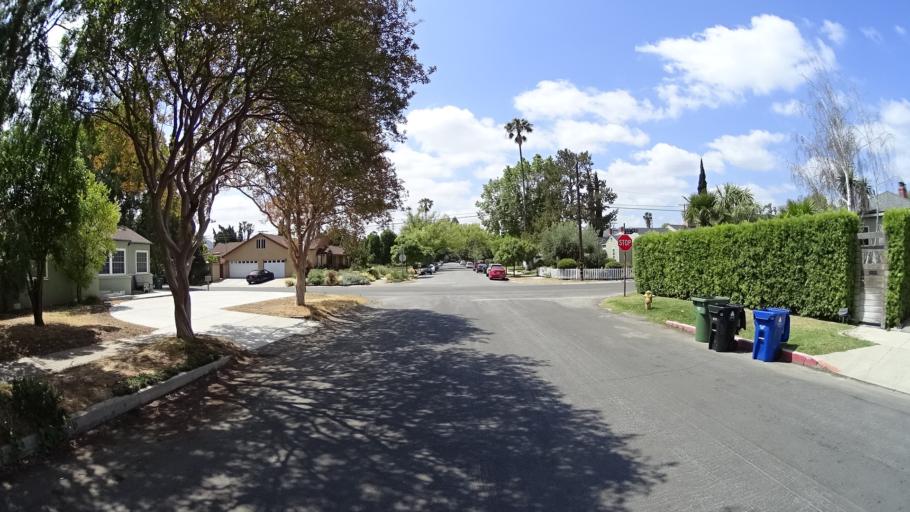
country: US
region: California
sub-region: Los Angeles County
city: Universal City
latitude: 34.1596
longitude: -118.3539
